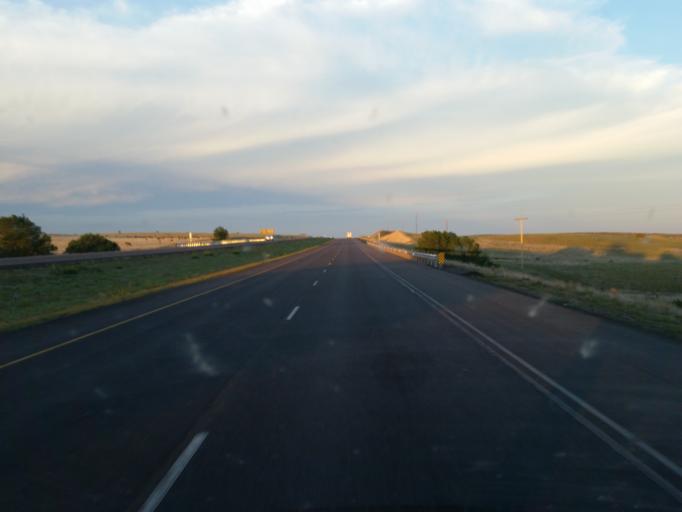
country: US
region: New Mexico
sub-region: Guadalupe County
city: Santa Rosa
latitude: 34.9907
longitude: -105.2792
